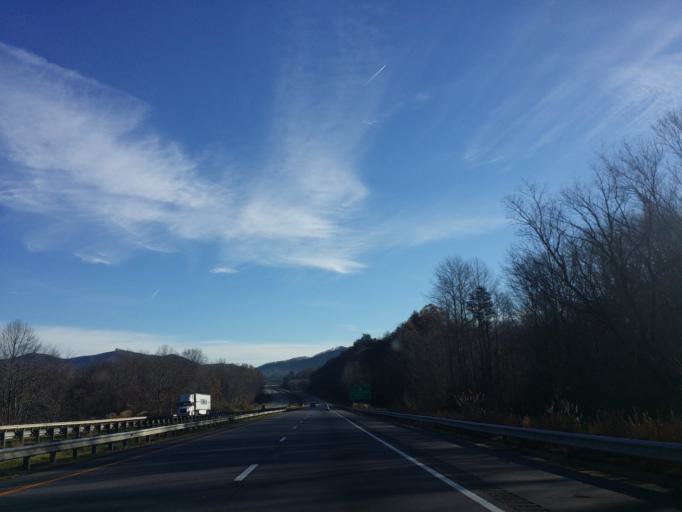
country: US
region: North Carolina
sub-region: Buncombe County
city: Black Mountain
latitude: 35.6016
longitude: -82.3581
